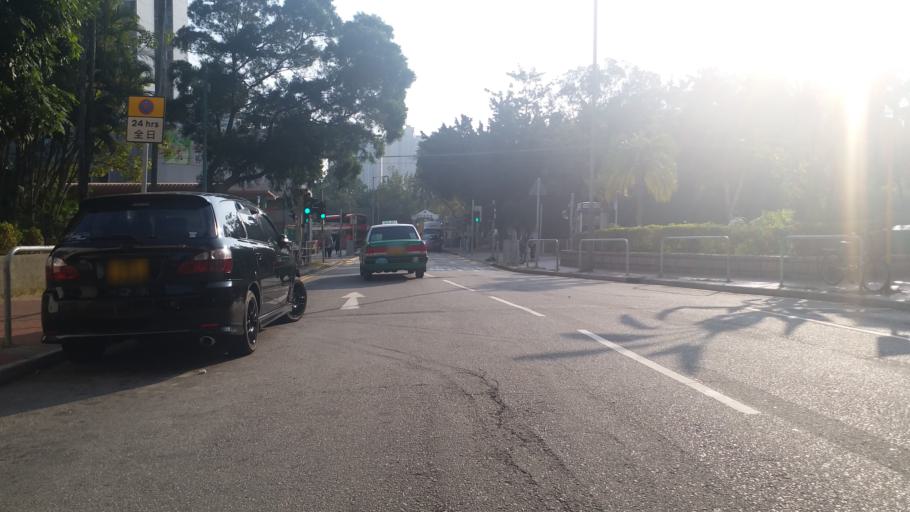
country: HK
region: Tuen Mun
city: Tuen Mun
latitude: 22.4072
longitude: 113.9691
